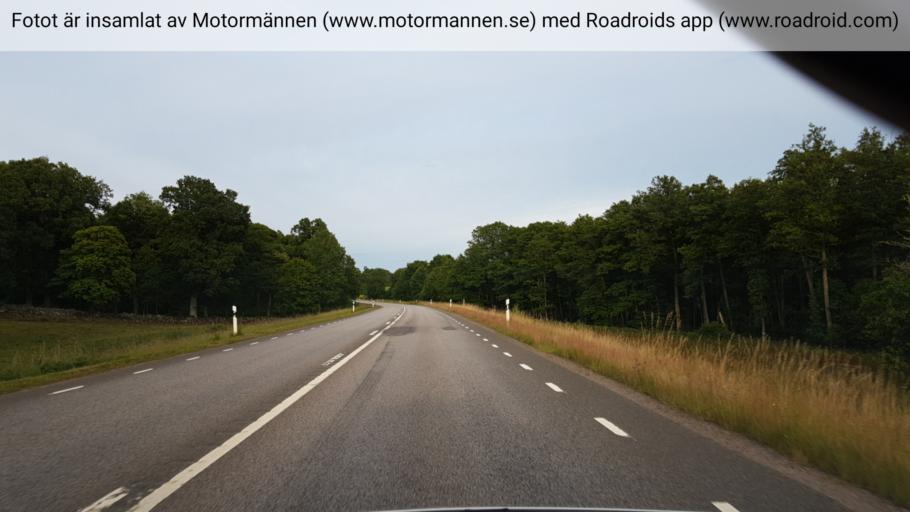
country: SE
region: Vaestra Goetaland
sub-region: Falkopings Kommun
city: Falkoeping
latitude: 58.2428
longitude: 13.5238
